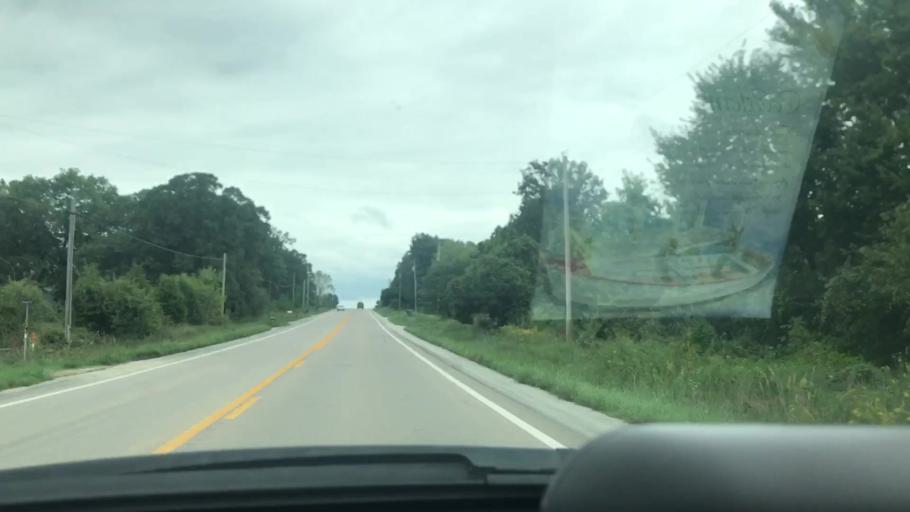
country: US
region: Missouri
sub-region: Dallas County
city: Buffalo
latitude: 37.7004
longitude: -93.1068
